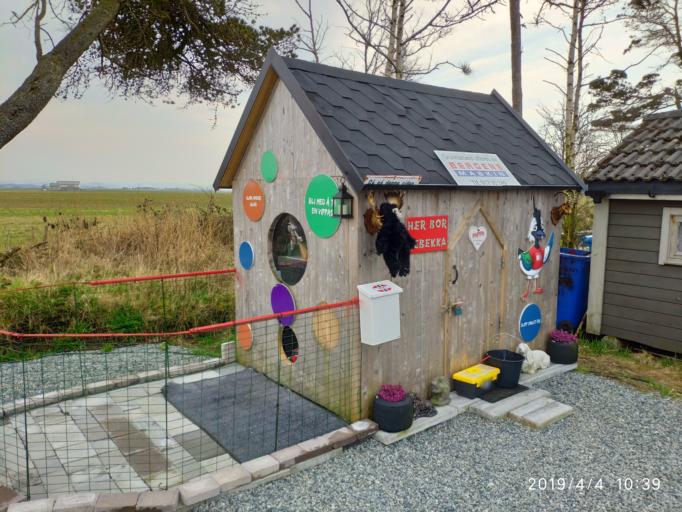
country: NO
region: Rogaland
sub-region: Klepp
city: Kleppe
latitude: 58.8014
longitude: 5.5579
